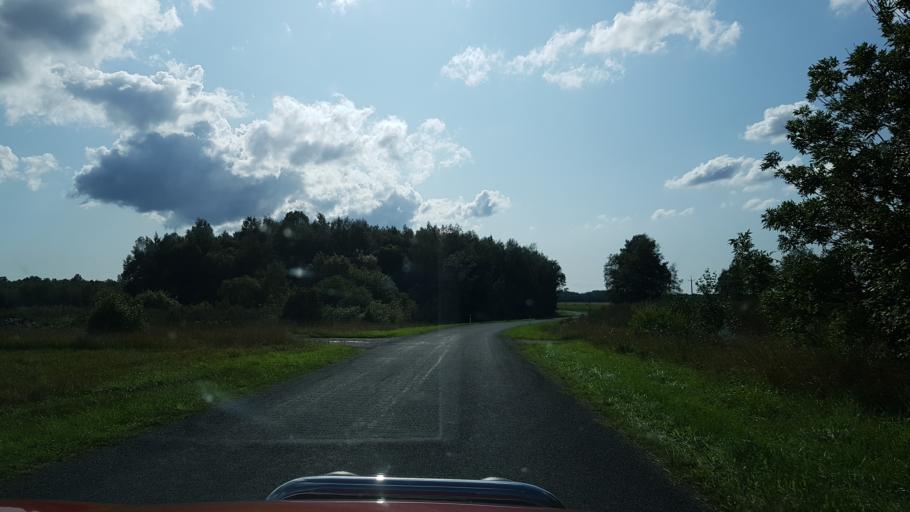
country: EE
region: Harju
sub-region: Paldiski linn
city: Paldiski
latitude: 59.2053
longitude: 23.9867
